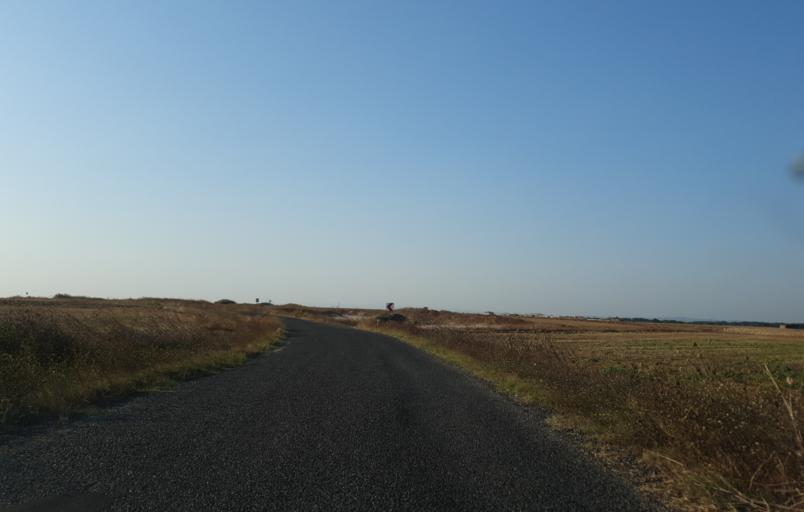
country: TR
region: Tekirdag
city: Beyazkoy
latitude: 41.4187
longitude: 27.7643
